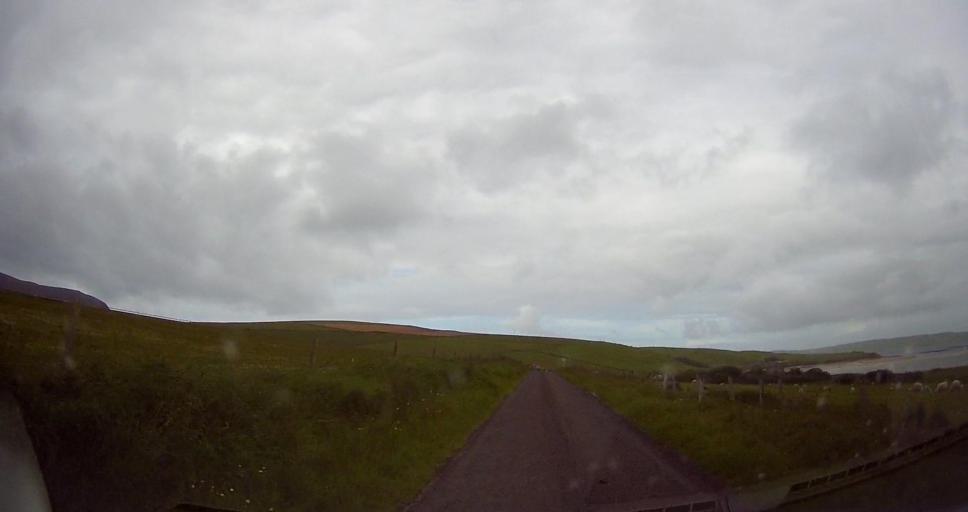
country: GB
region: Scotland
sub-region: Orkney Islands
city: Stromness
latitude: 58.9131
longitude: -3.3226
